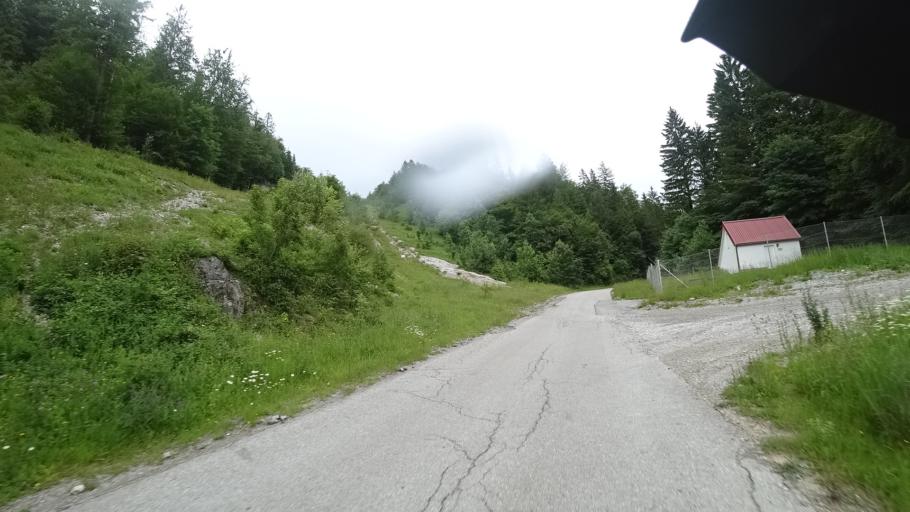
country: HR
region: Primorsko-Goranska
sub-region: Grad Delnice
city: Delnice
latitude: 45.3955
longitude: 14.8114
